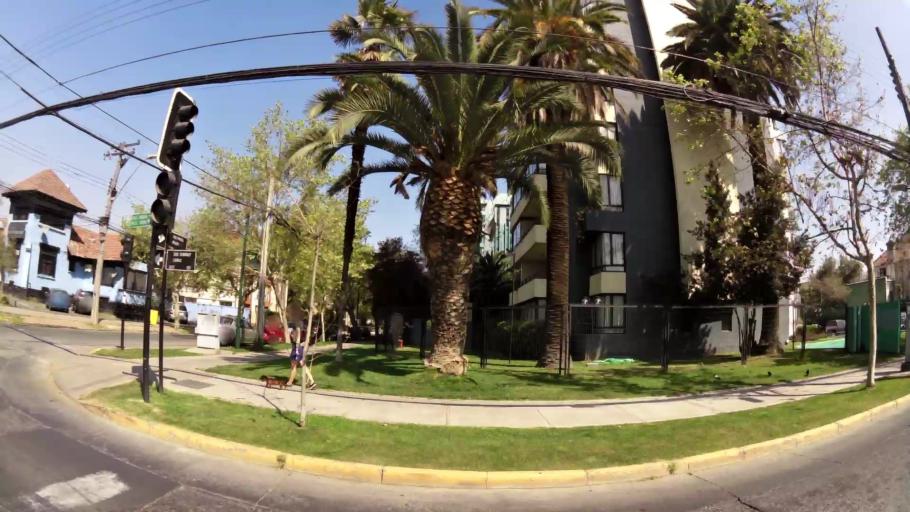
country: CL
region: Santiago Metropolitan
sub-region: Provincia de Santiago
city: Santiago
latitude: -33.4559
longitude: -70.6182
